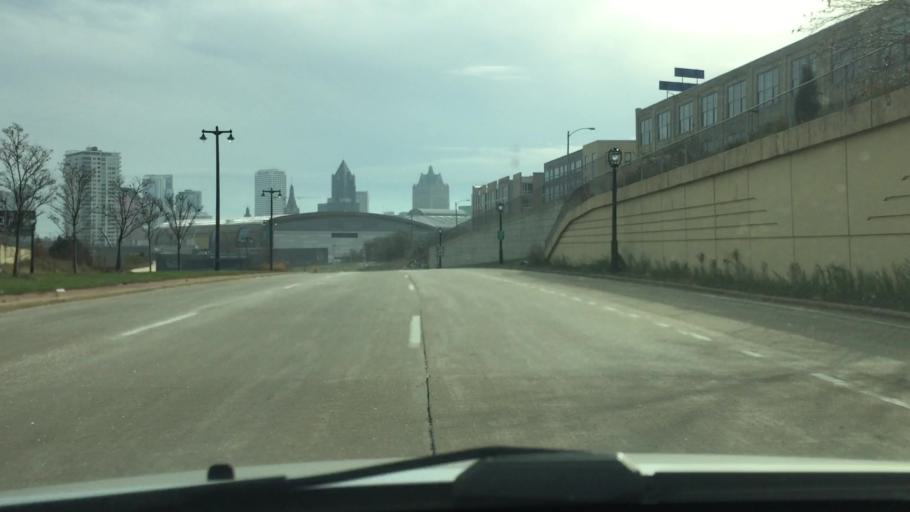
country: US
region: Wisconsin
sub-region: Milwaukee County
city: Milwaukee
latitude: 43.0479
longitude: -87.9236
